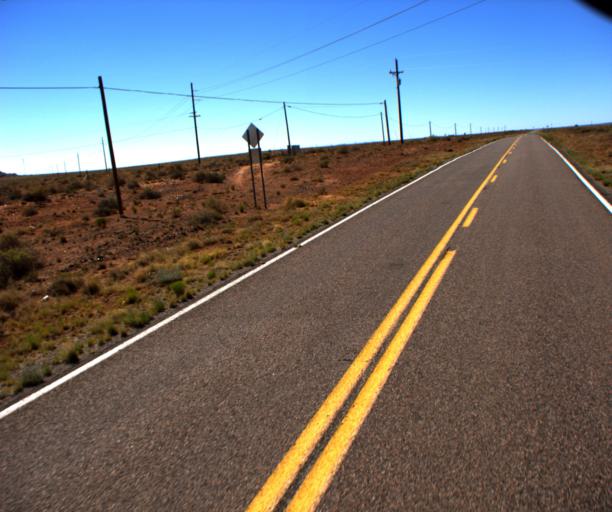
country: US
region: Arizona
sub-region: Coconino County
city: LeChee
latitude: 35.0830
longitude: -110.8623
